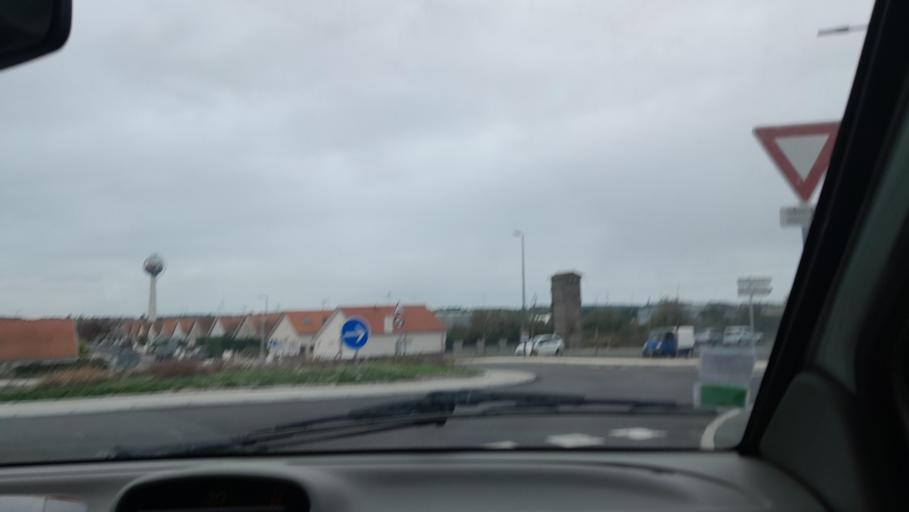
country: FR
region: Pays de la Loire
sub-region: Departement de la Loire-Atlantique
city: Saint-Mars-la-Jaille
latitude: 47.5150
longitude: -1.1835
